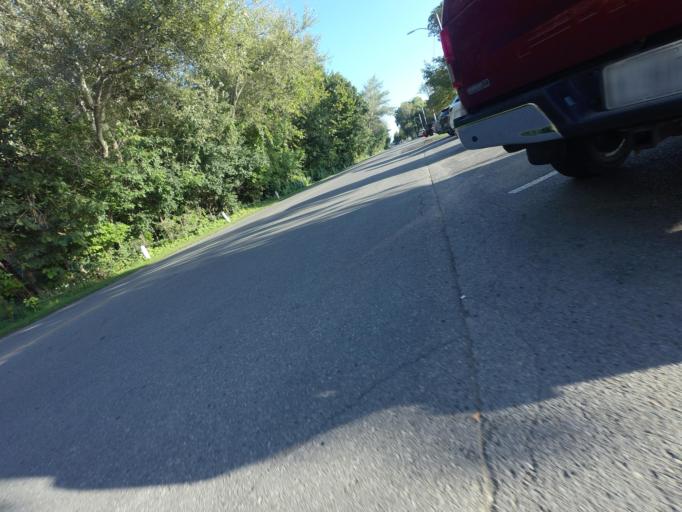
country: CA
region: Ontario
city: Goderich
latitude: 43.7418
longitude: -81.7260
